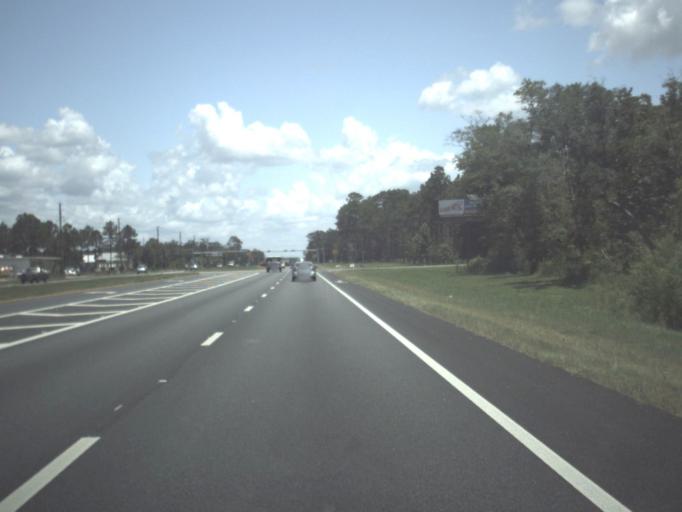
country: US
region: Florida
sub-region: Walton County
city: Freeport
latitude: 30.4830
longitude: -86.1242
